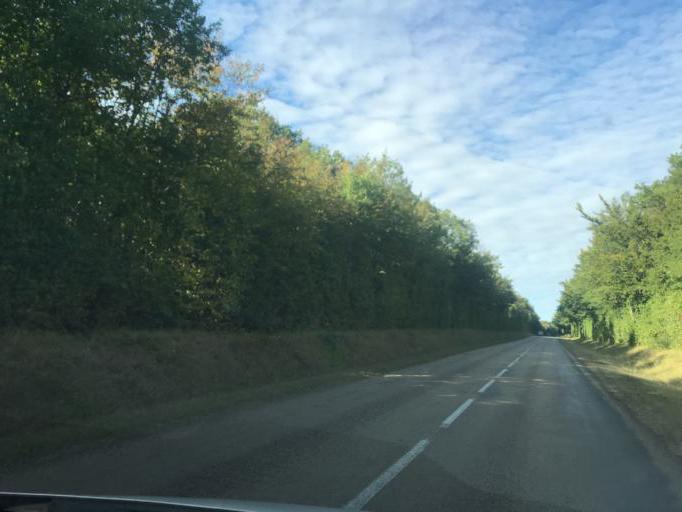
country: FR
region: Bourgogne
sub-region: Departement de l'Yonne
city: Fontenailles
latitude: 47.5728
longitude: 3.4546
